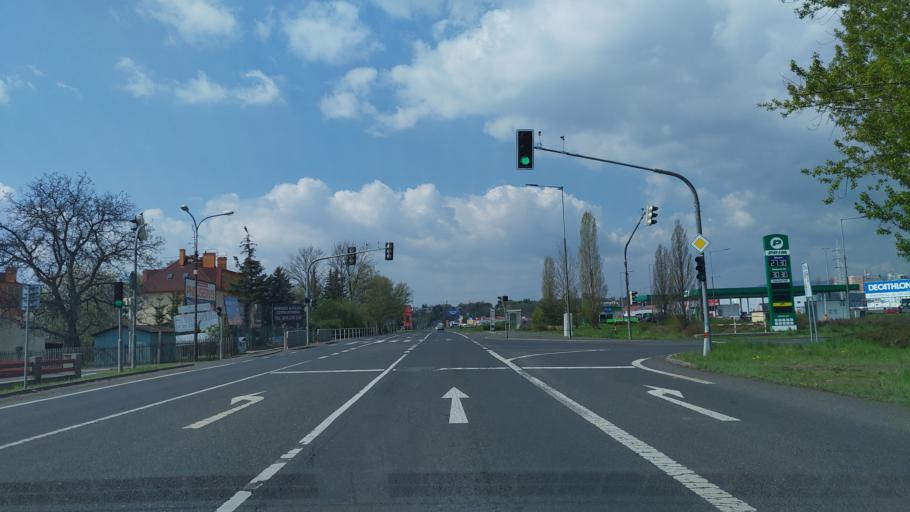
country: CZ
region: Ustecky
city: Krupka
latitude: 50.6605
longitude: 13.8687
